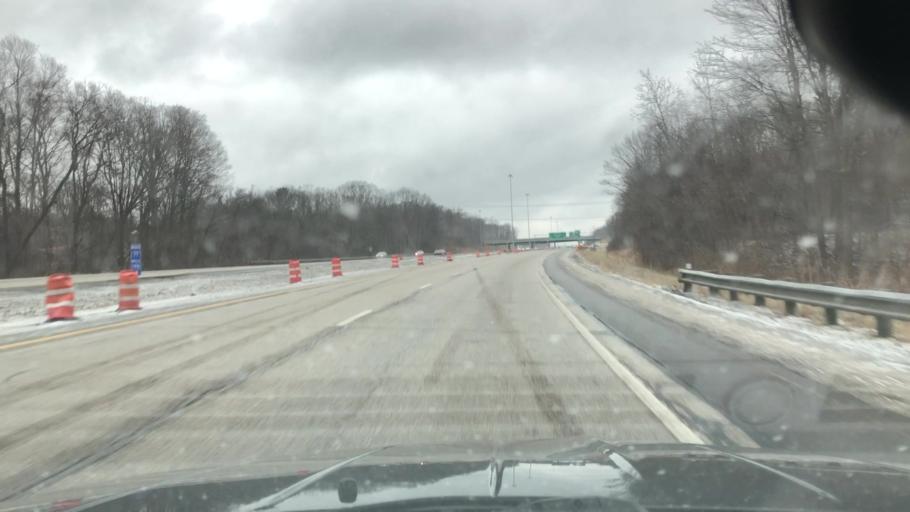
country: US
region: Ohio
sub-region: Summit County
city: Richfield
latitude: 41.2676
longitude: -81.6361
